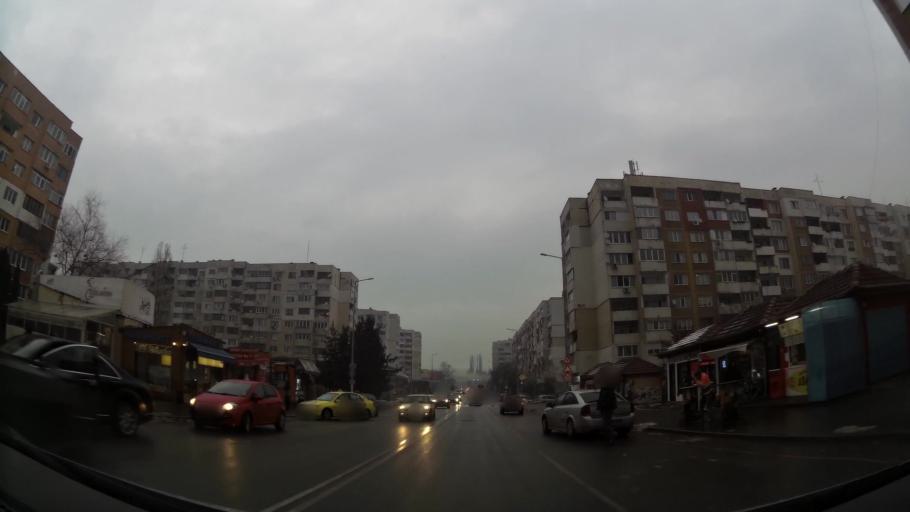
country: BG
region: Sofia-Capital
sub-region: Stolichna Obshtina
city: Sofia
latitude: 42.6878
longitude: 23.2552
